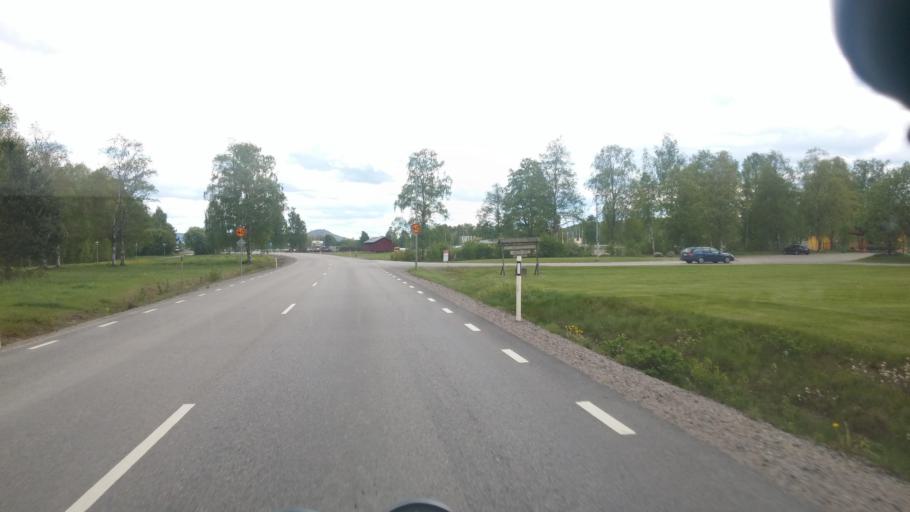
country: SE
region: Gaevleborg
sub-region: Ljusdals Kommun
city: Ljusdal
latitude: 61.8219
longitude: 16.0790
